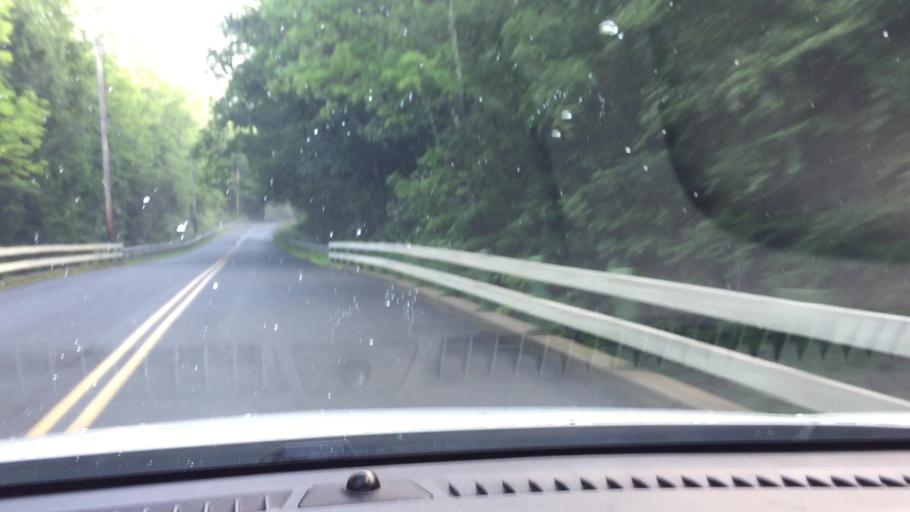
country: US
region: Massachusetts
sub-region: Berkshire County
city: Becket
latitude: 42.3975
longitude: -72.9801
